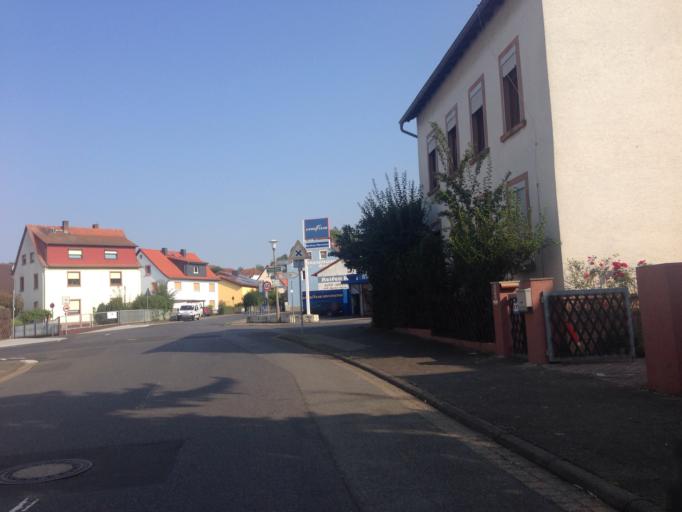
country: DE
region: Hesse
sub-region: Regierungsbezirk Darmstadt
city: Maintal
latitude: 50.1543
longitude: 8.8076
